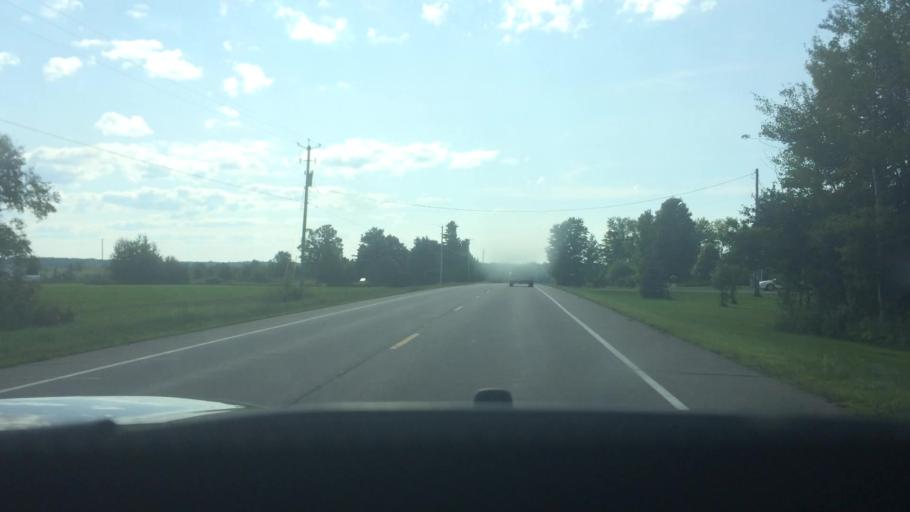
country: US
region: New York
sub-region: Franklin County
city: Malone
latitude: 44.8451
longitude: -74.1778
